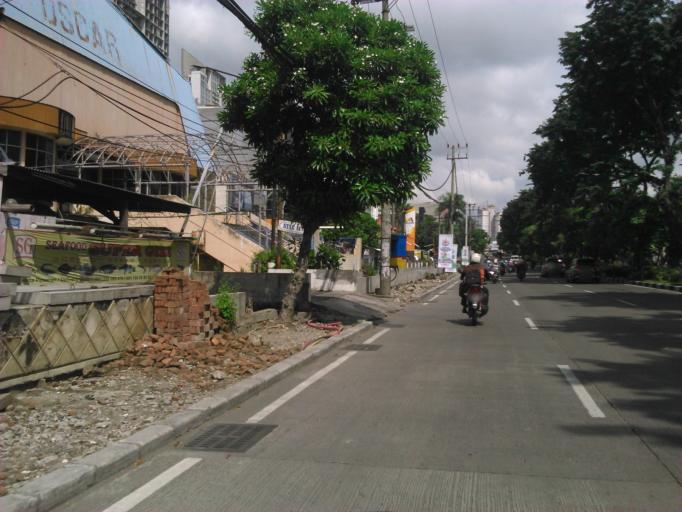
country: ID
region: East Java
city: Jagirsidosermo
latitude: -7.2922
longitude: 112.7238
